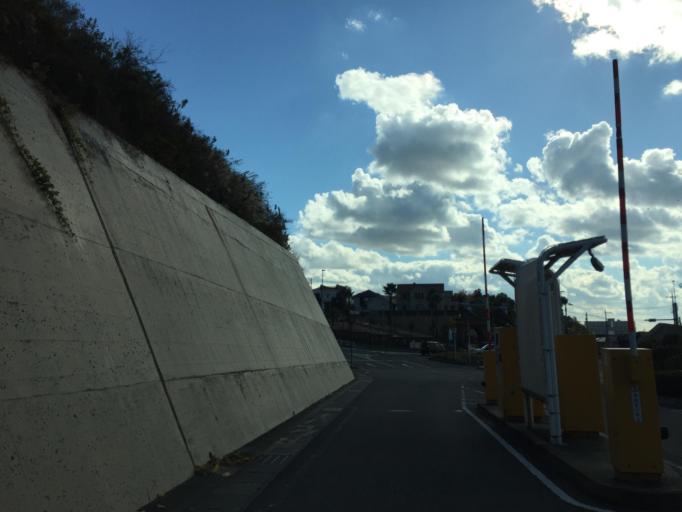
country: JP
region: Wakayama
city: Wakayama-shi
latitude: 34.2743
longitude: 135.1503
